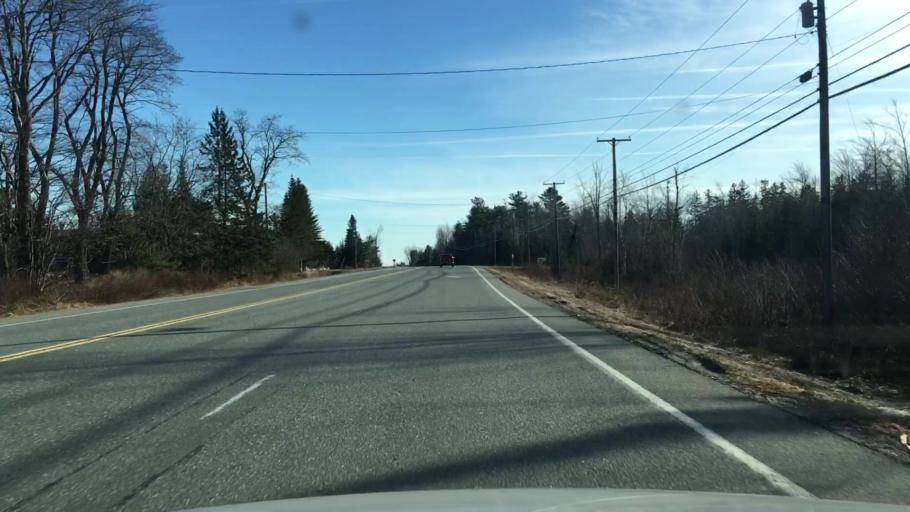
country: US
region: Maine
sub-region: Hancock County
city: Surry
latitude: 44.6220
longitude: -68.5313
